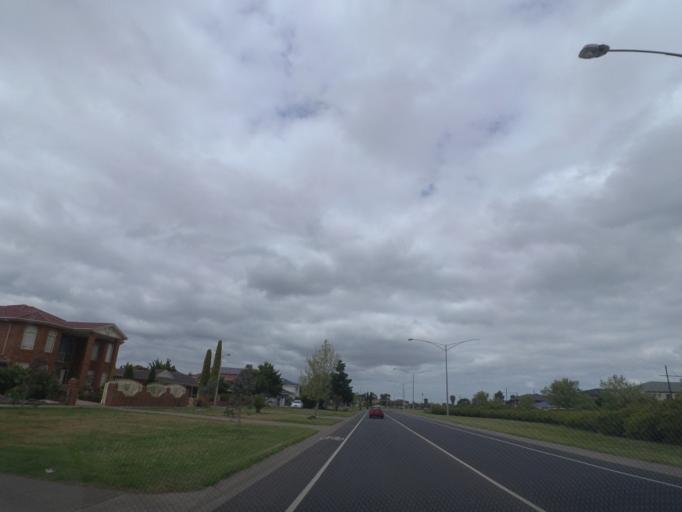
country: AU
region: Victoria
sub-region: Melton
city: Caroline Springs
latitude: -37.7543
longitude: 144.7536
